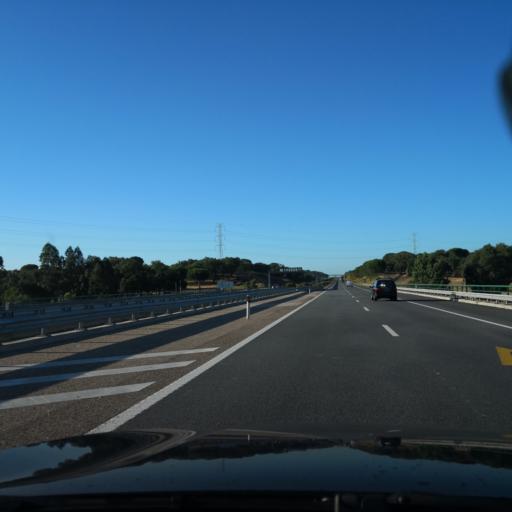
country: PT
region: Evora
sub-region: Vendas Novas
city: Vendas Novas
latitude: 38.5794
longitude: -8.6208
